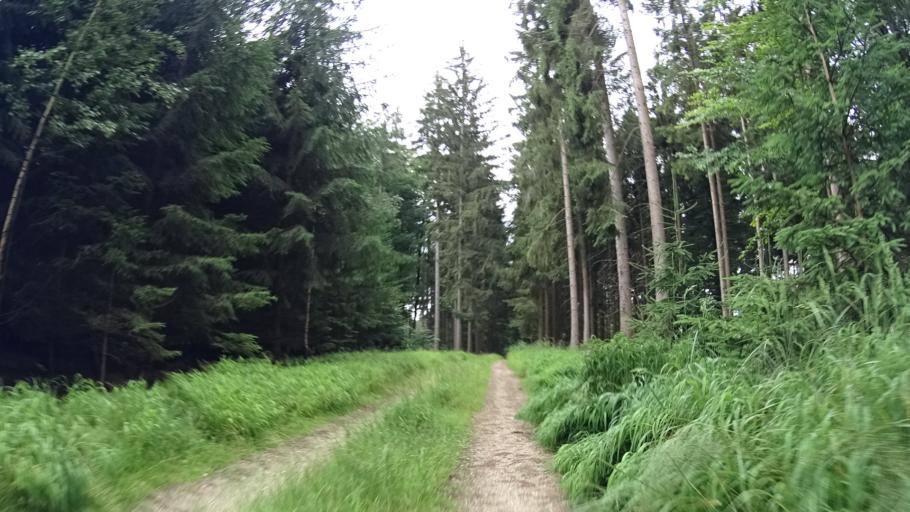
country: DE
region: Bavaria
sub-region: Upper Bavaria
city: Denkendorf
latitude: 48.9099
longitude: 11.4832
